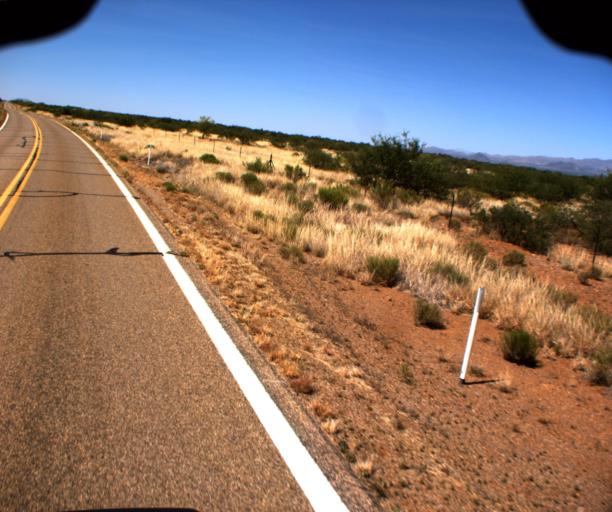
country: US
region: Arizona
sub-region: Pima County
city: Three Points
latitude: 31.6919
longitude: -111.4870
